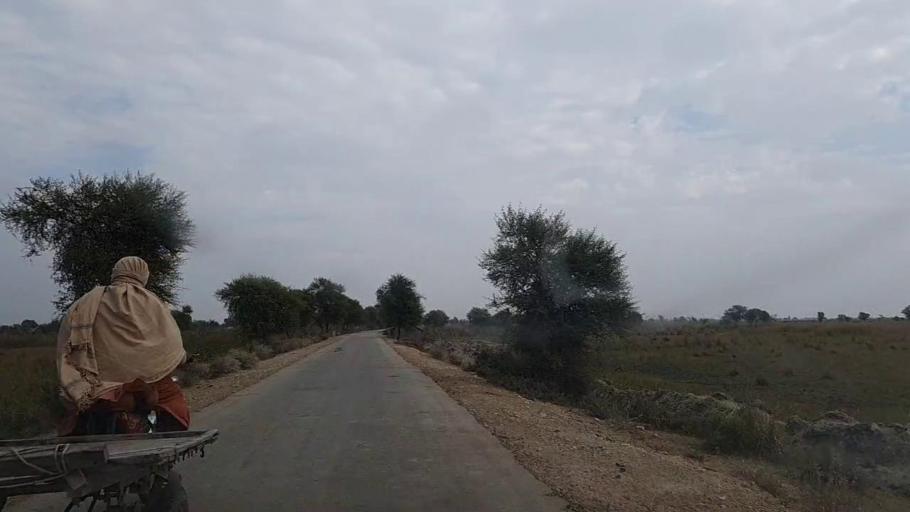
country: PK
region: Sindh
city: Sanghar
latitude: 26.2286
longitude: 69.0085
